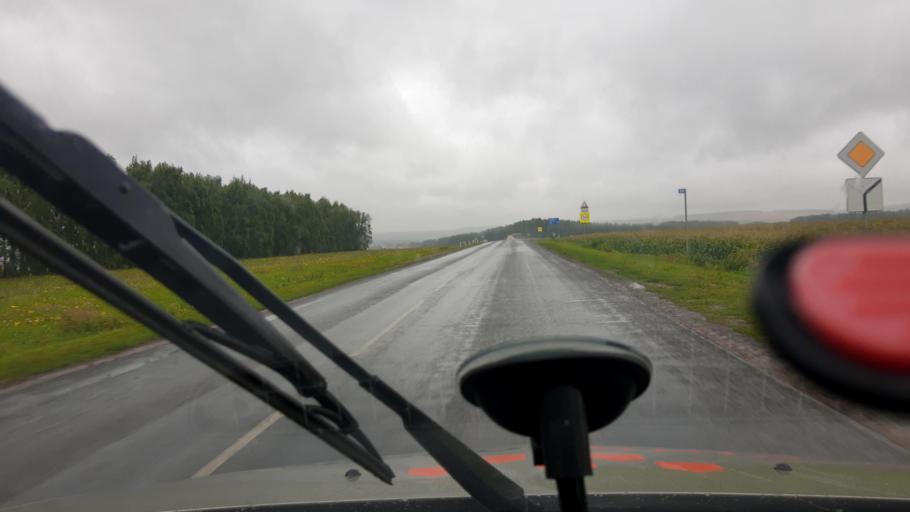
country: RU
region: Bashkortostan
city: Chekmagush
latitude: 55.1056
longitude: 54.6498
